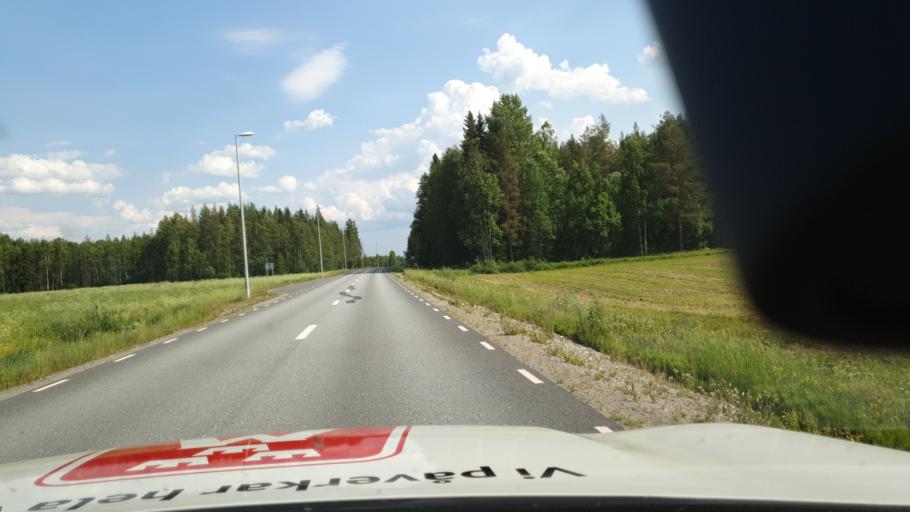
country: SE
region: Vaesterbotten
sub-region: Skelleftea Kommun
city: Forsbacka
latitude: 64.6948
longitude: 20.4897
